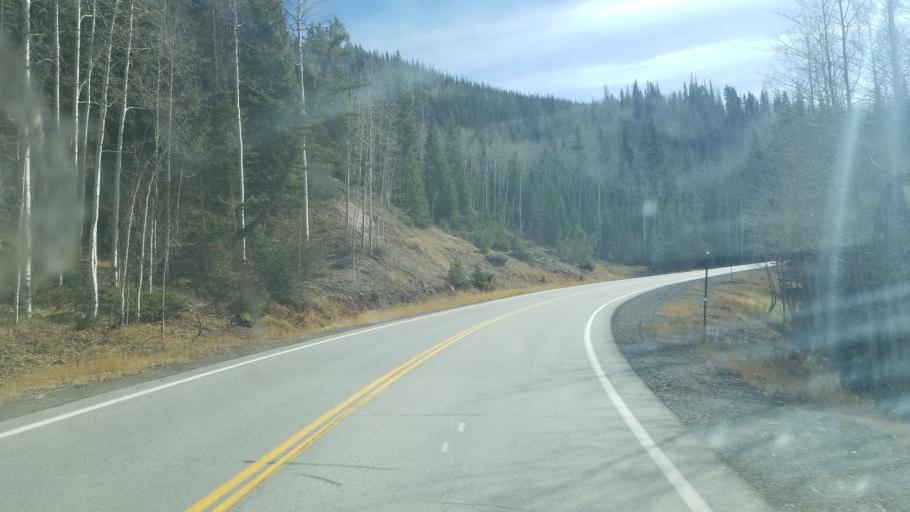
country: US
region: New Mexico
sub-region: Rio Arriba County
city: Chama
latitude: 37.1062
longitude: -106.3694
